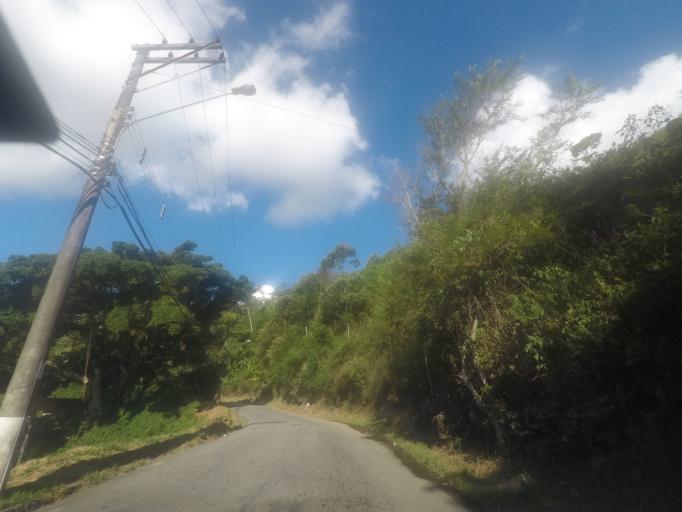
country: BR
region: Rio de Janeiro
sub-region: Petropolis
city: Petropolis
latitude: -22.5076
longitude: -43.1577
